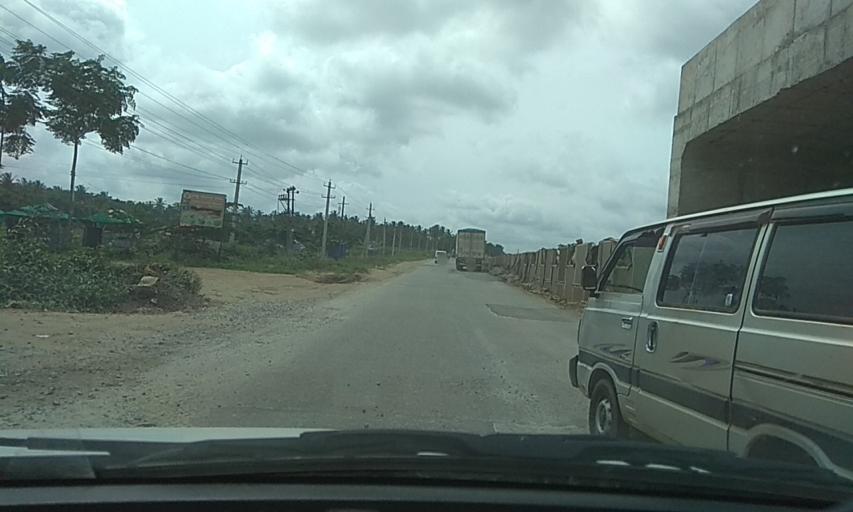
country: IN
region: Karnataka
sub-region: Davanagere
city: Mayakonda
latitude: 14.4256
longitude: 75.9739
